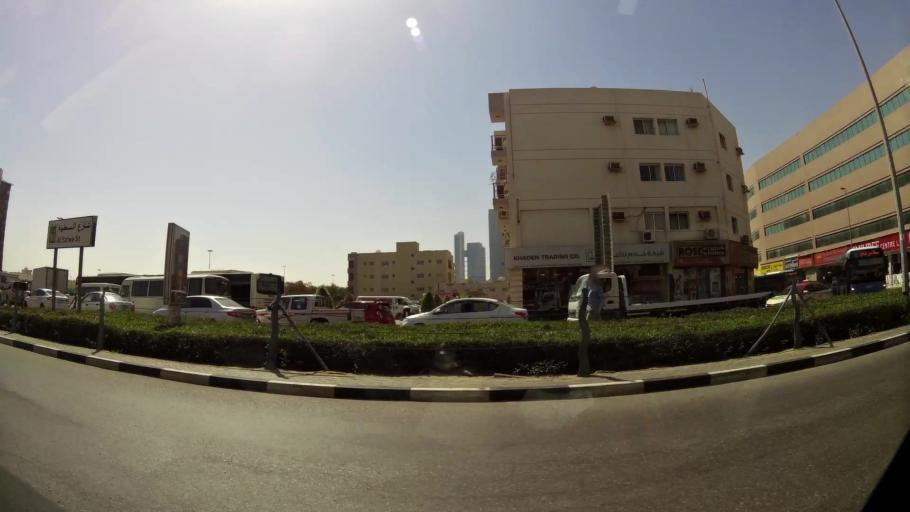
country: AE
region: Ash Shariqah
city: Sharjah
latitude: 25.2343
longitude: 55.2783
